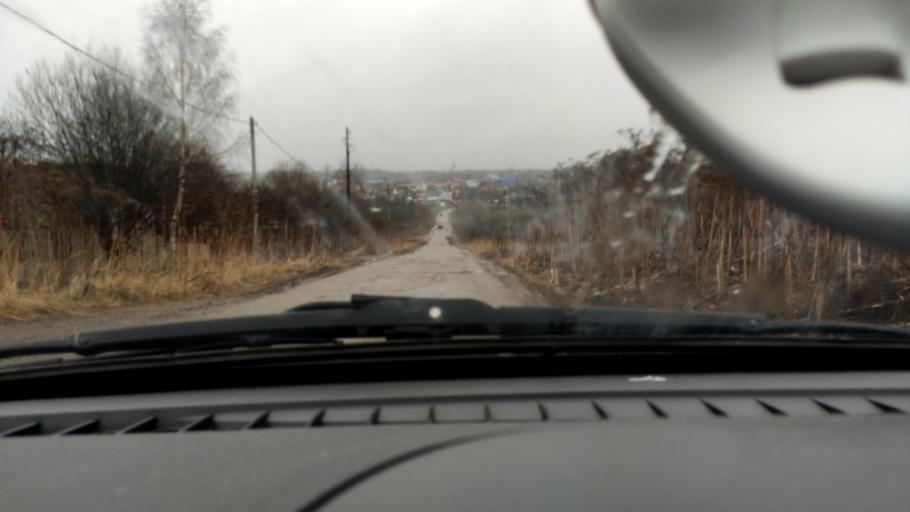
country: RU
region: Perm
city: Perm
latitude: 58.0336
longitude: 56.4120
